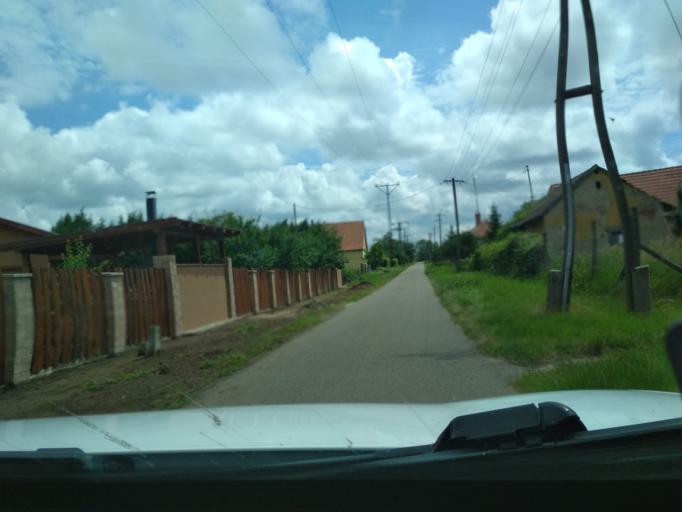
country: HU
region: Jasz-Nagykun-Szolnok
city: Tiszafured
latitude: 47.6065
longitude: 20.7245
